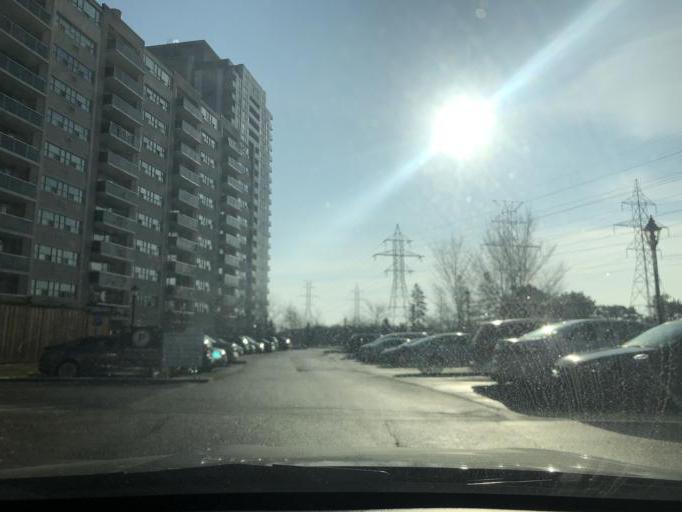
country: CA
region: Ontario
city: Etobicoke
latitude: 43.6759
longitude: -79.5662
